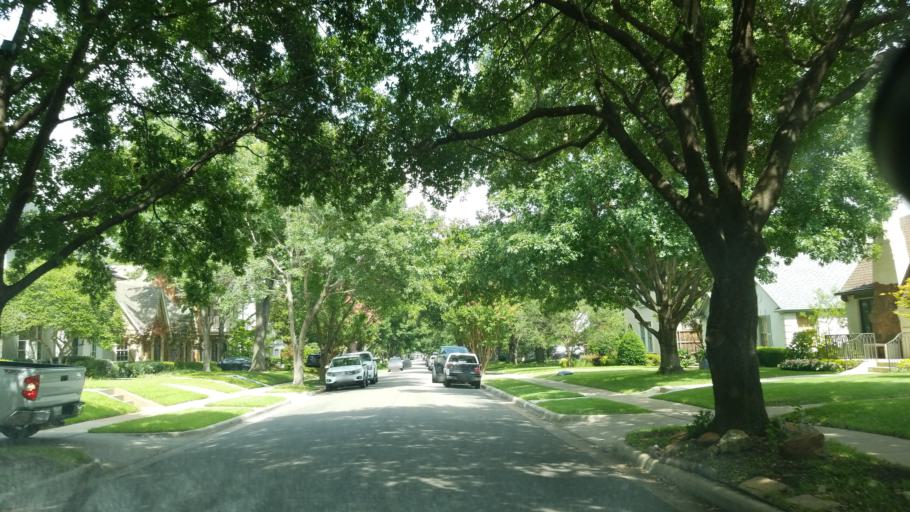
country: US
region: Texas
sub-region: Dallas County
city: University Park
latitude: 32.8521
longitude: -96.8030
